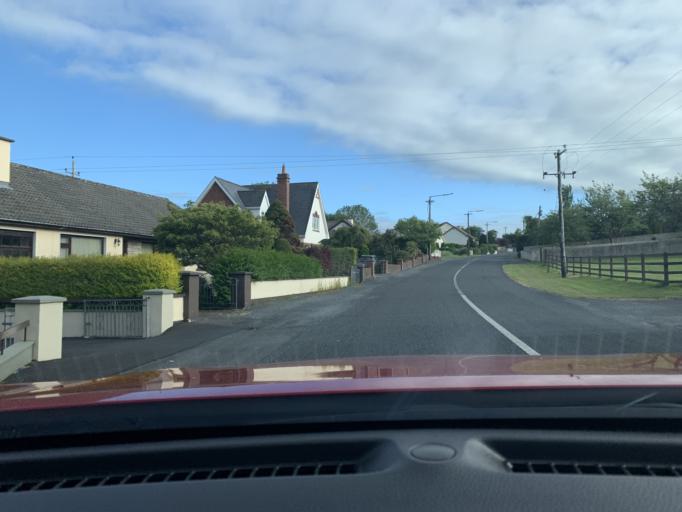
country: IE
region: Connaught
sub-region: Sligo
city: Sligo
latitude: 54.2720
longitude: -8.5238
